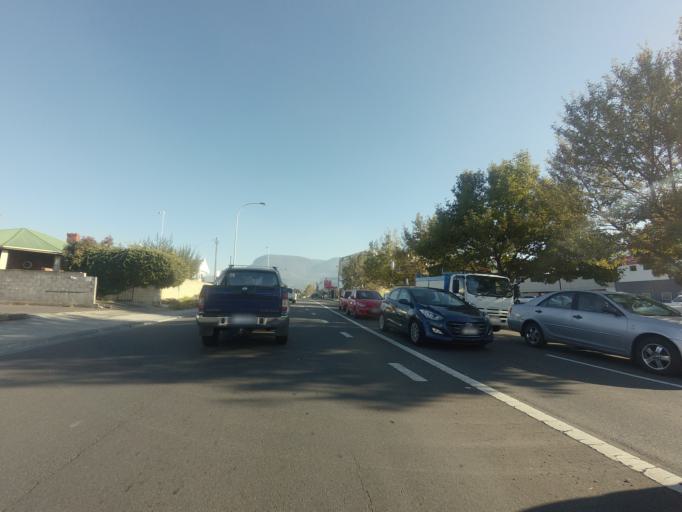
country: AU
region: Tasmania
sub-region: Glenorchy
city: Glenorchy
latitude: -42.8339
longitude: 147.2787
